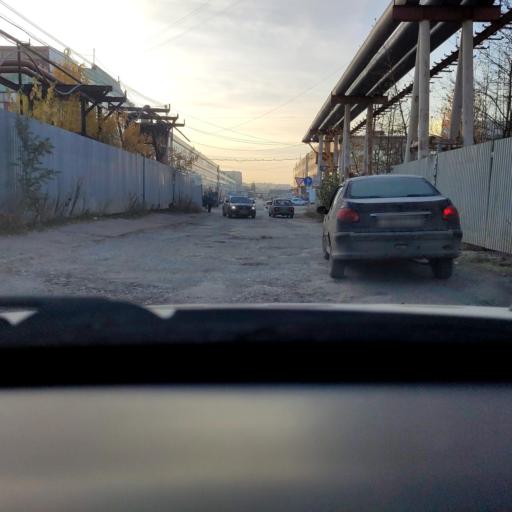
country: RU
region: Perm
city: Froly
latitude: 57.9621
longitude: 56.2723
